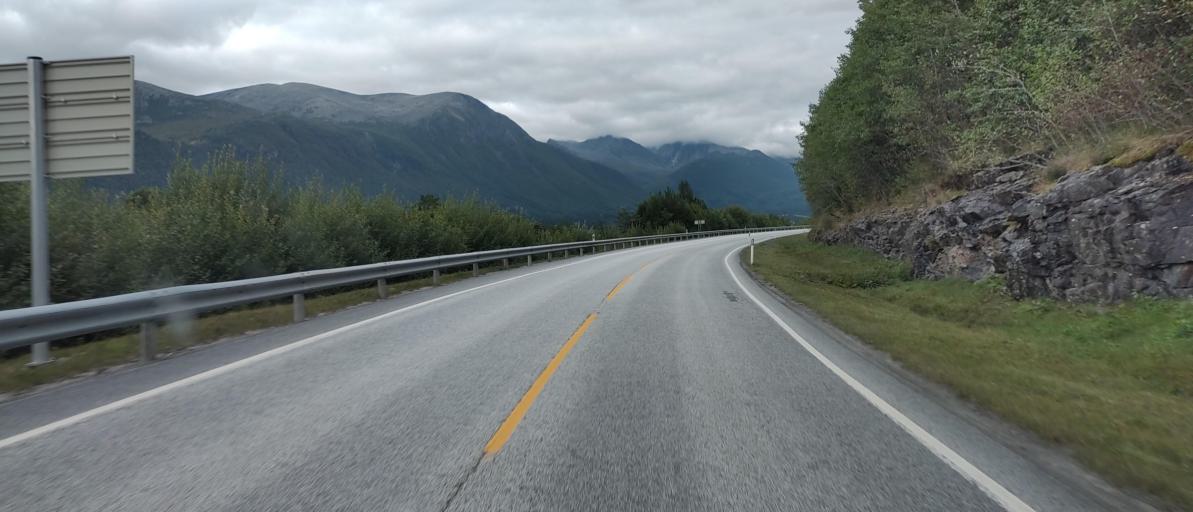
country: NO
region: More og Romsdal
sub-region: Rauma
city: Andalsnes
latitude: 62.5660
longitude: 7.6995
